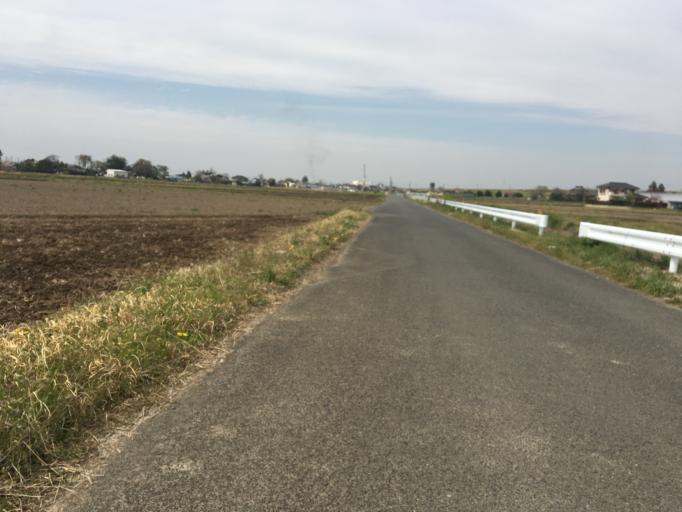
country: JP
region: Saitama
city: Shiki
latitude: 35.8619
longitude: 139.5751
